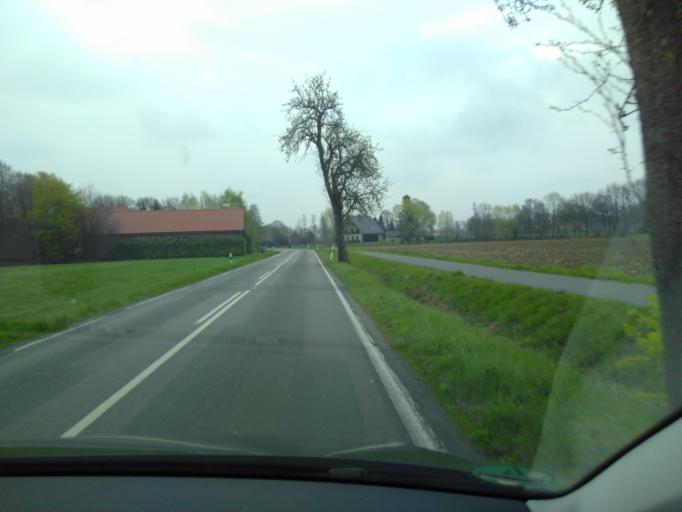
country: DE
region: North Rhine-Westphalia
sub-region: Regierungsbezirk Detmold
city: Verl
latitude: 51.8507
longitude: 8.5458
